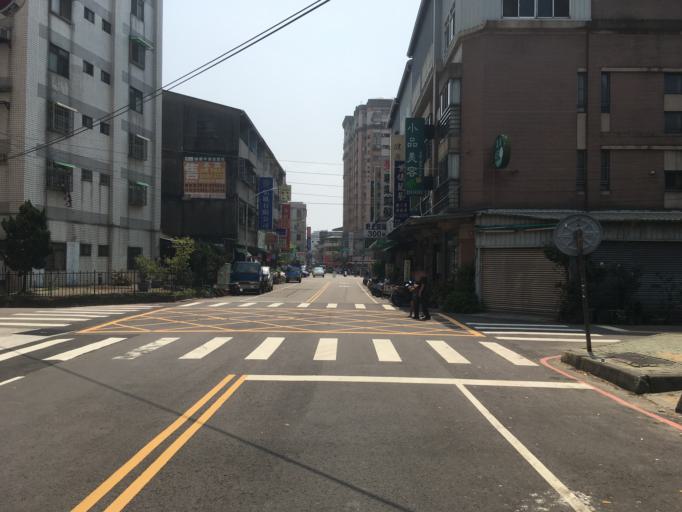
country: TW
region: Taiwan
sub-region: Taichung City
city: Taichung
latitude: 24.1844
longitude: 120.6963
